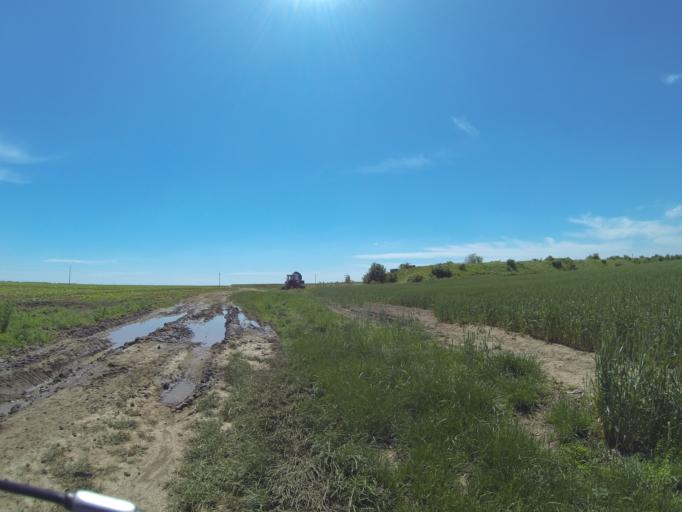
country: RO
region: Dolj
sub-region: Comuna Leu
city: Zanoaga
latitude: 44.2022
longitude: 24.0651
